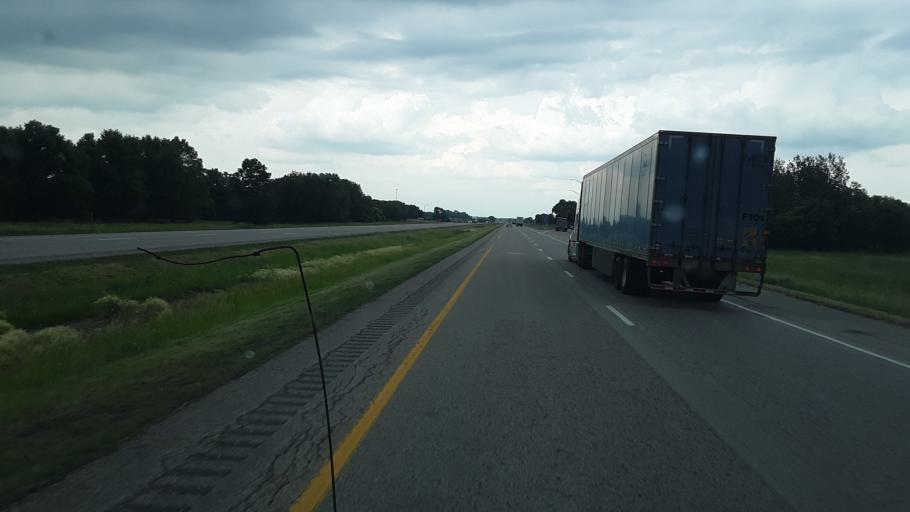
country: US
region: Iowa
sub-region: Pottawattamie County
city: Council Bluffs
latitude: 41.3980
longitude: -95.6633
